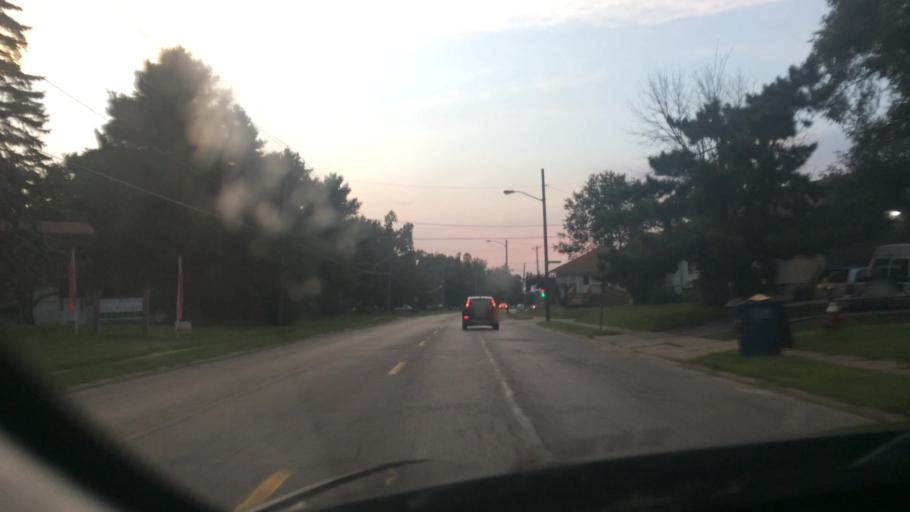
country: US
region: Ohio
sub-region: Lucas County
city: Ottawa Hills
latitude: 41.7095
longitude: -83.6080
